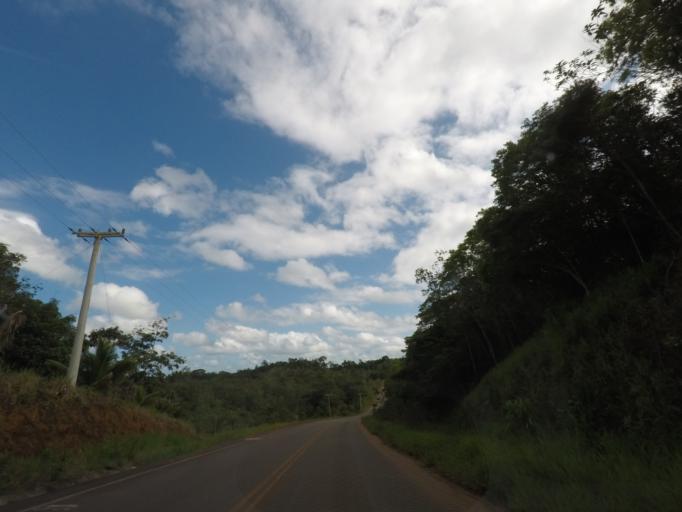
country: BR
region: Bahia
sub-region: Itacare
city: Itacare
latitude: -14.2200
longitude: -39.0986
